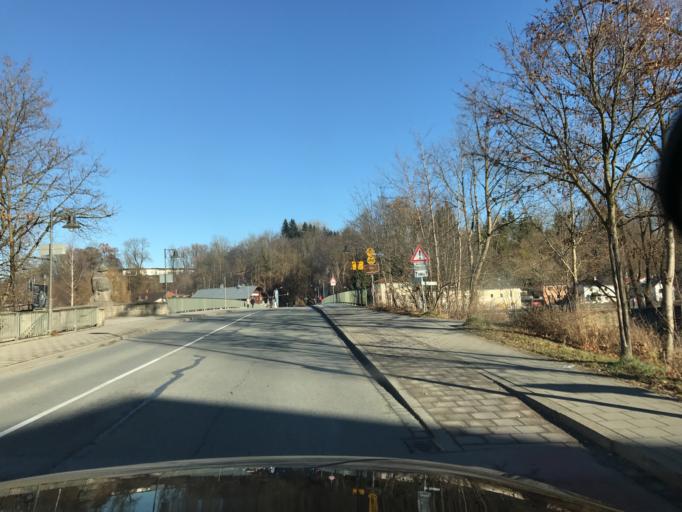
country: DE
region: Bavaria
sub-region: Upper Bavaria
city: Rosenheim
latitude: 47.8552
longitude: 12.1407
